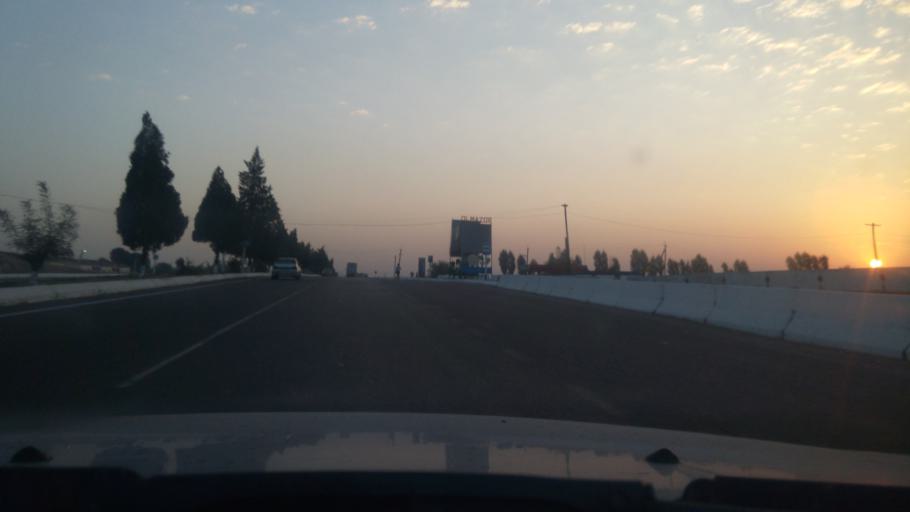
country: UZ
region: Toshkent
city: Zafar
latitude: 41.0122
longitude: 68.8411
